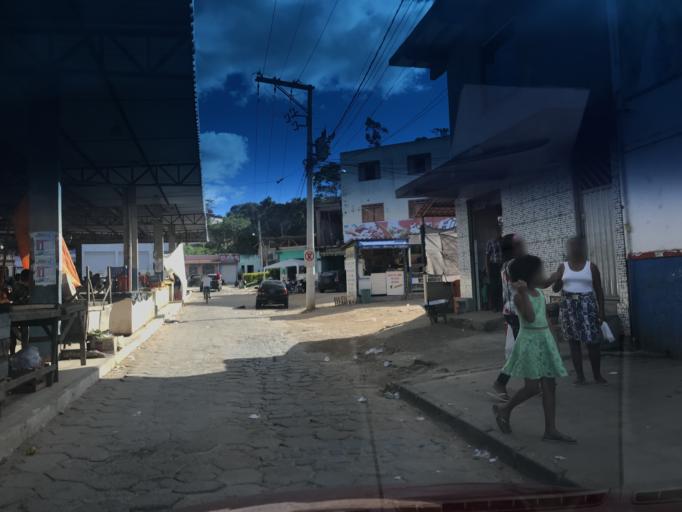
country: BR
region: Bahia
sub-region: Gandu
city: Gandu
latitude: -13.7436
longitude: -39.4901
